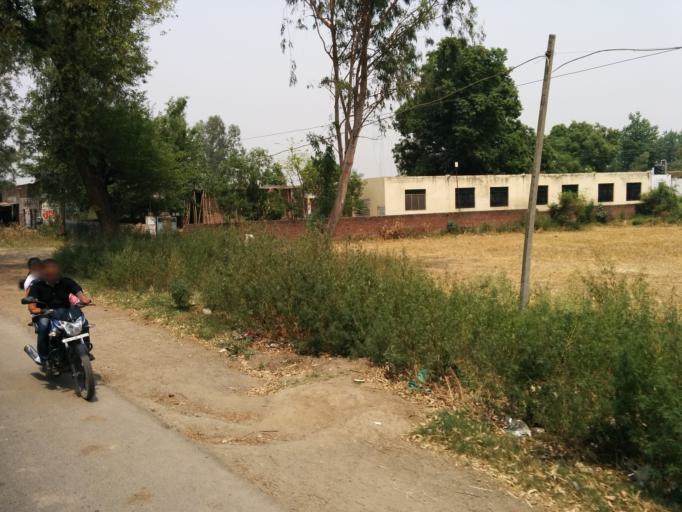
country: IN
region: Punjab
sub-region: Gurdaspur
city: Dhariwal
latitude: 31.9328
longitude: 75.3058
